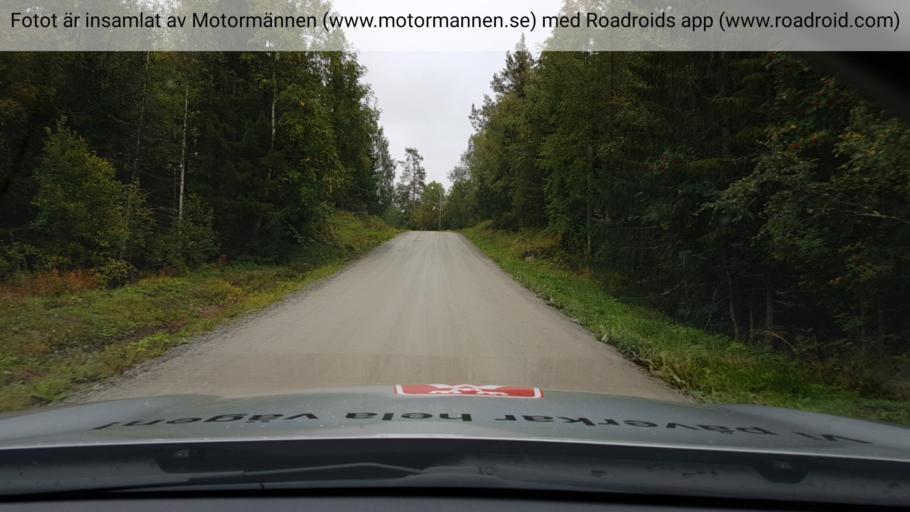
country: SE
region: Jaemtland
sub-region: Braecke Kommun
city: Braecke
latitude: 62.7703
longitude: 15.4856
